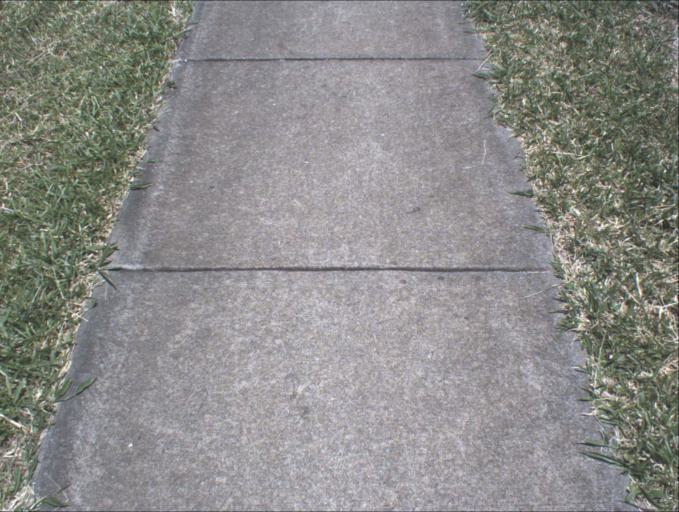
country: AU
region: Queensland
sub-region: Logan
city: Rochedale South
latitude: -27.5994
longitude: 153.1046
